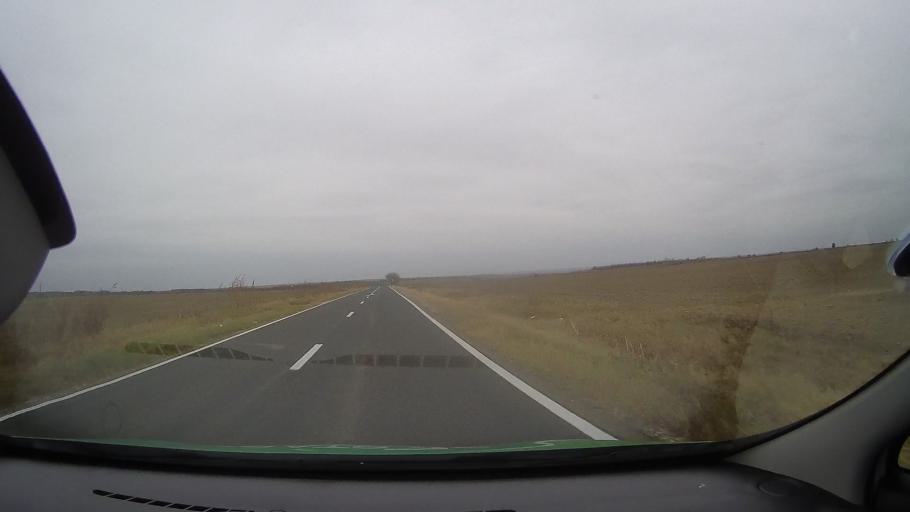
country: RO
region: Constanta
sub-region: Comuna Garliciu
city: Garliciu
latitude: 44.7107
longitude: 28.0857
